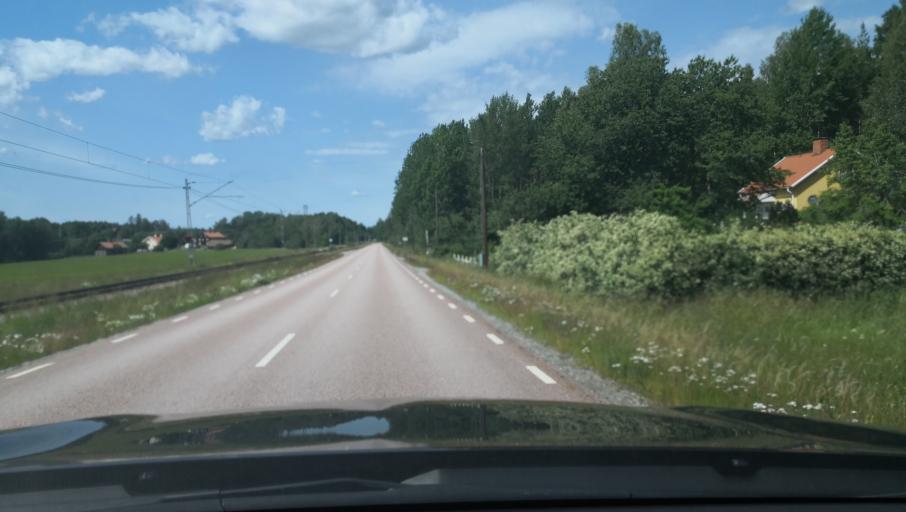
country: SE
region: Vaestmanland
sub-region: Surahammars Kommun
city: Ramnas
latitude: 59.8190
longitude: 16.1540
